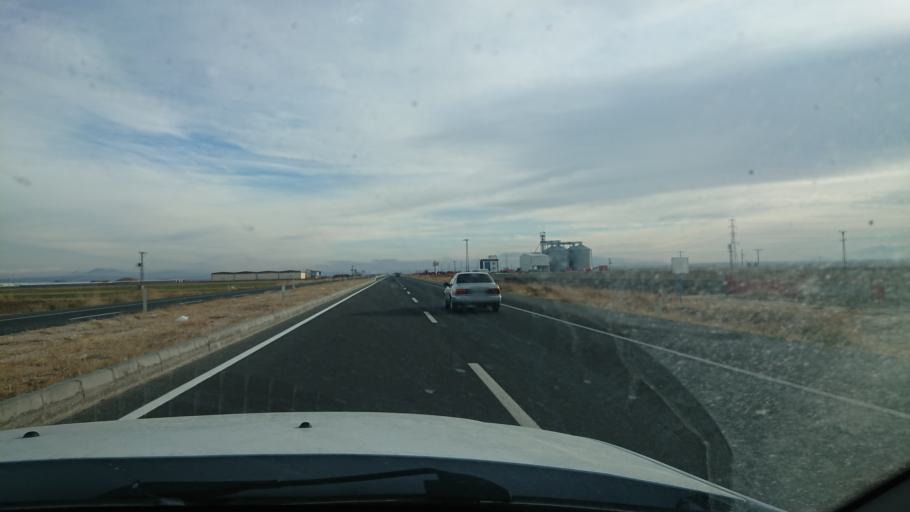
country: TR
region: Aksaray
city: Yesilova
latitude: 38.3057
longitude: 33.8146
